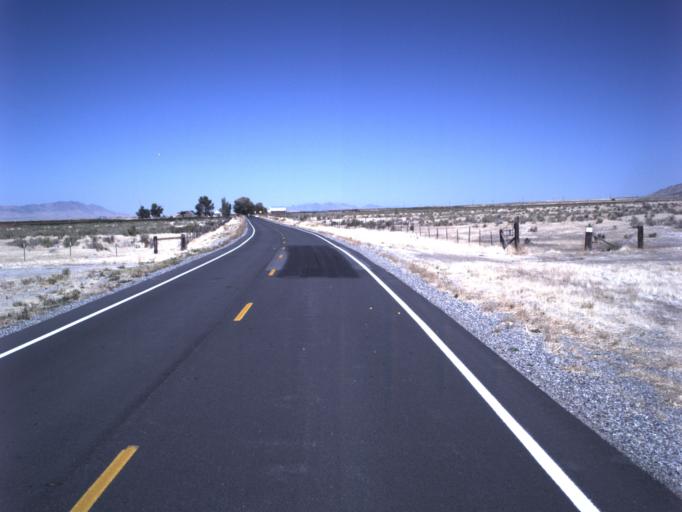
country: US
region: Utah
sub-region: Tooele County
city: Grantsville
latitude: 40.4840
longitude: -112.7456
